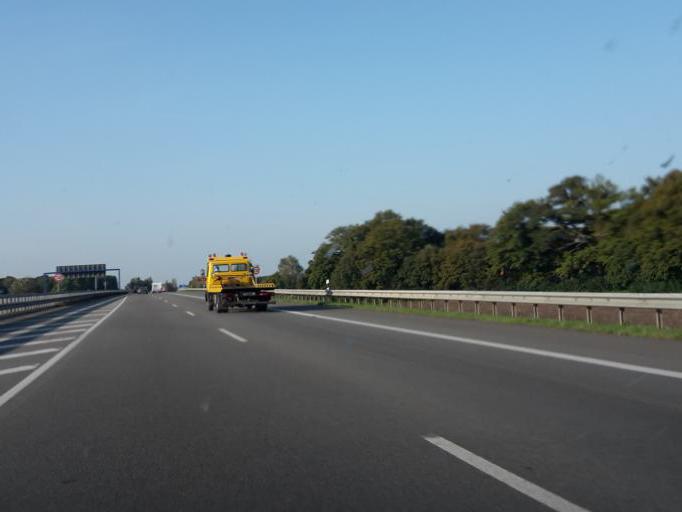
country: DE
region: Lower Saxony
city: Wallenhorst
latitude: 52.4015
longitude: 8.0352
